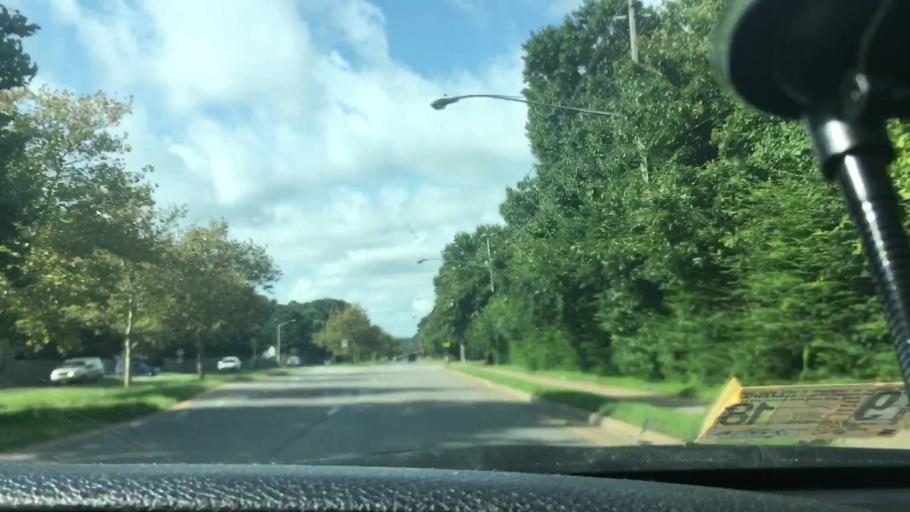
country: US
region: Virginia
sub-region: City of Virginia Beach
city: Virginia Beach
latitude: 36.8710
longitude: -76.0408
